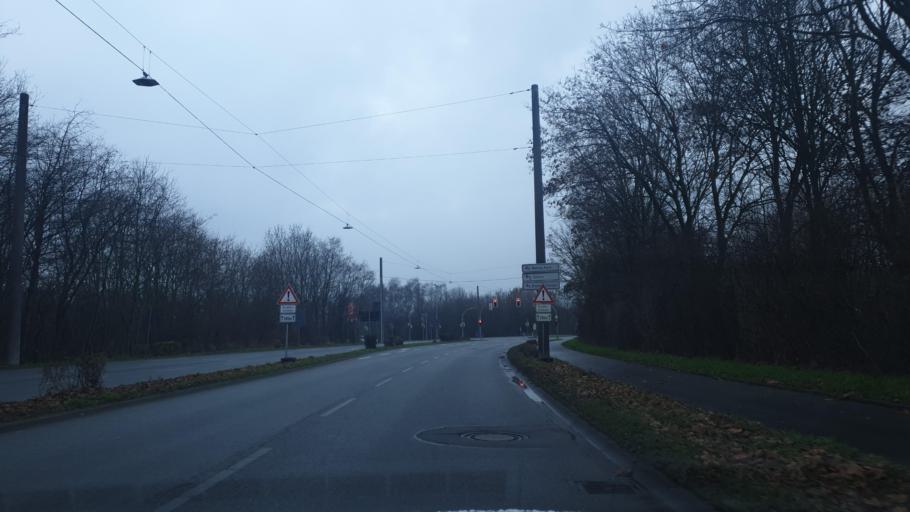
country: DE
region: North Rhine-Westphalia
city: Bad Oeynhausen
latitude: 52.2160
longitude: 8.8197
